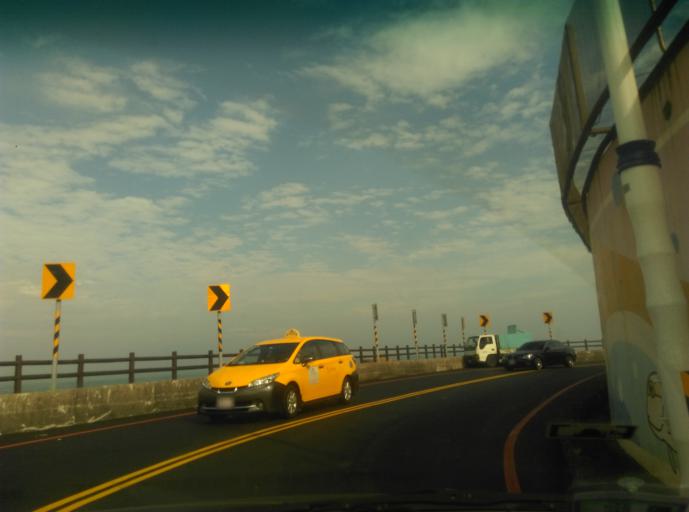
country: TW
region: Taiwan
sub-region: Keelung
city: Keelung
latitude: 25.1631
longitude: 121.7296
